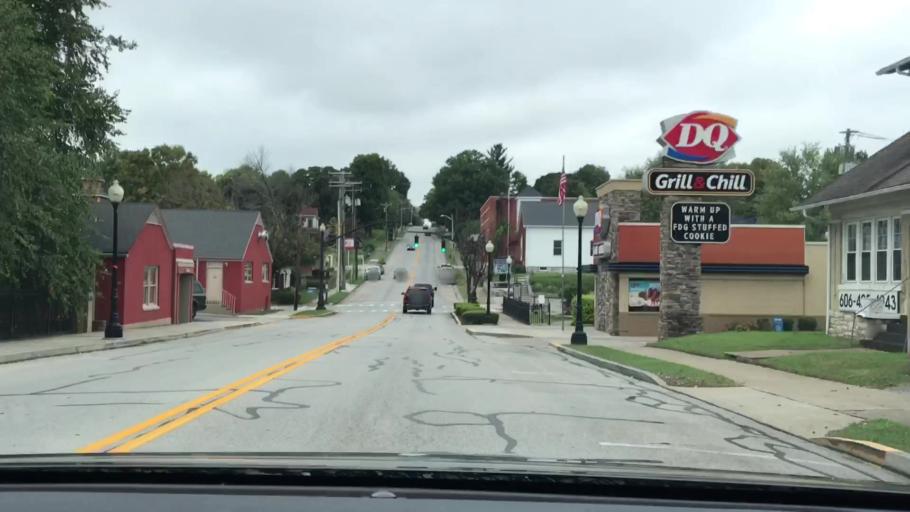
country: US
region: Kentucky
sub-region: Pulaski County
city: Somerset
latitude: 37.0945
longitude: -84.6055
